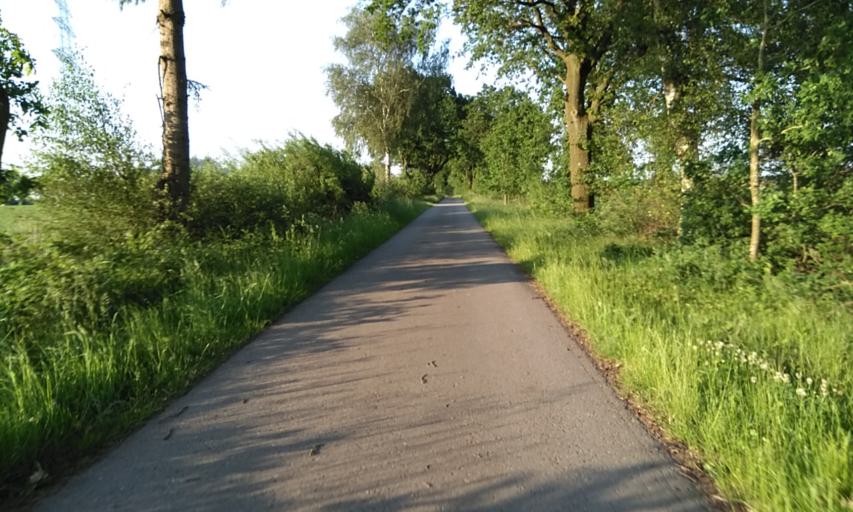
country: DE
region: Lower Saxony
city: Dollern
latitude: 53.5338
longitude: 9.5241
